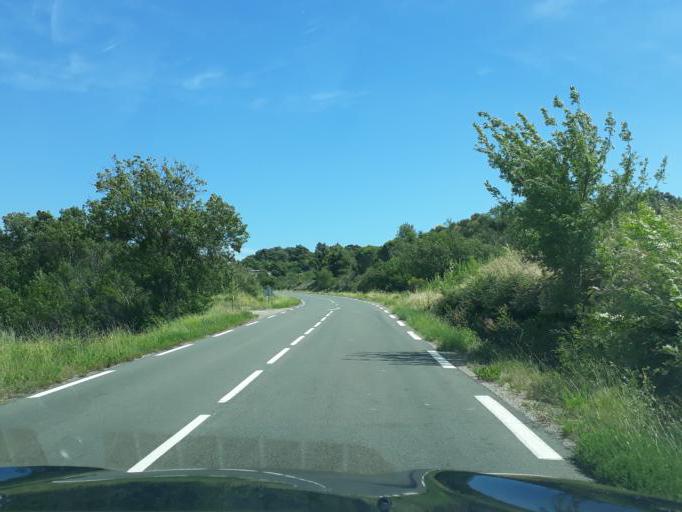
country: FR
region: Languedoc-Roussillon
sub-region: Departement de l'Aude
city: Portel-des-Corbieres
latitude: 43.0448
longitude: 2.9285
